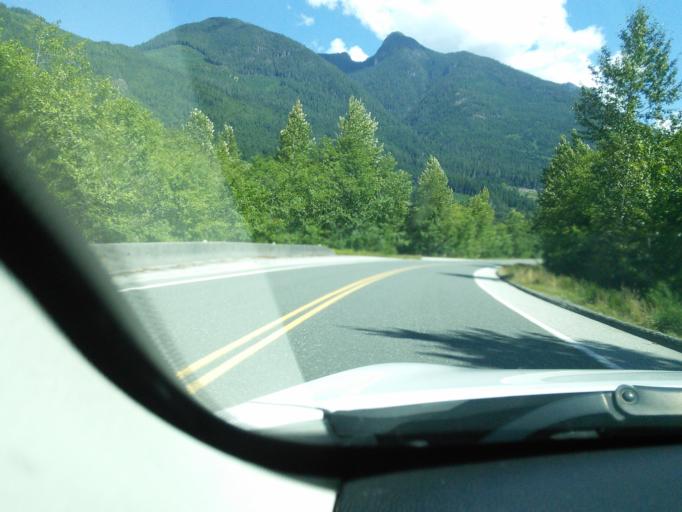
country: CA
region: British Columbia
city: Campbell River
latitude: 50.3608
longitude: -125.9158
